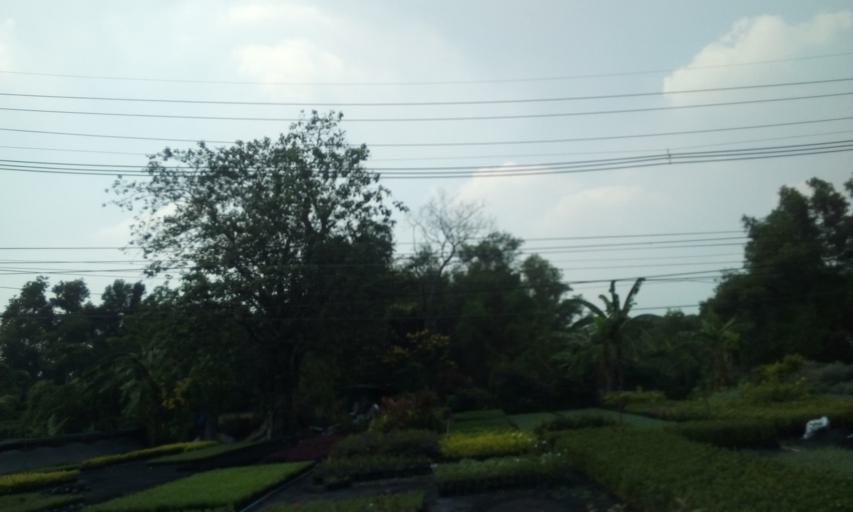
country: TH
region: Nakhon Nayok
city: Ongkharak
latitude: 14.1251
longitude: 100.9429
